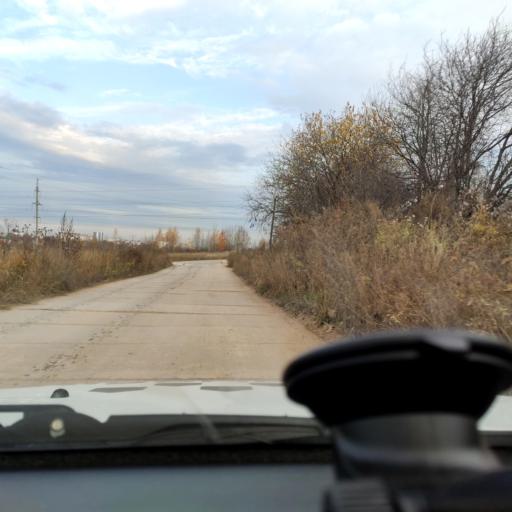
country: RU
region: Perm
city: Perm
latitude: 58.0136
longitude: 56.3290
